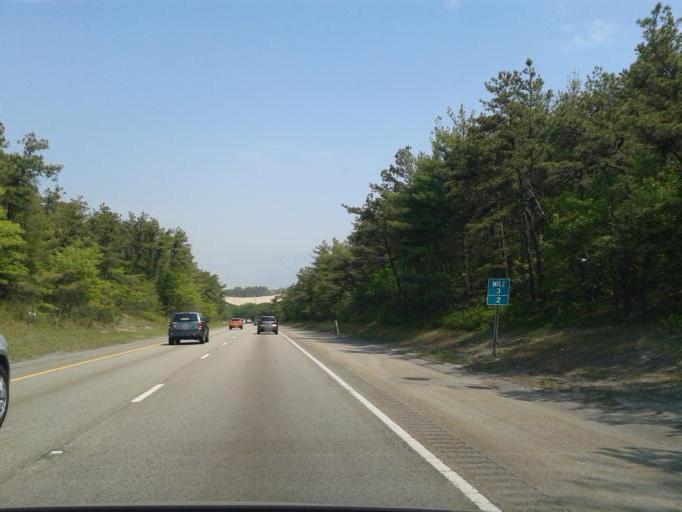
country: US
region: Massachusetts
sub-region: Barnstable County
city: Sagamore
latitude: 41.8235
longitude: -70.5581
